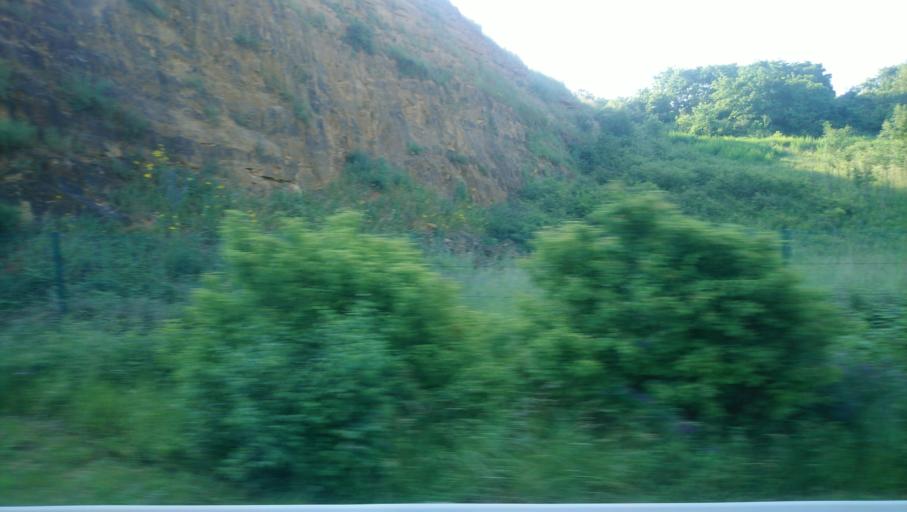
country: LU
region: Luxembourg
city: Aspelt
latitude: 49.5166
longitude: 6.2480
